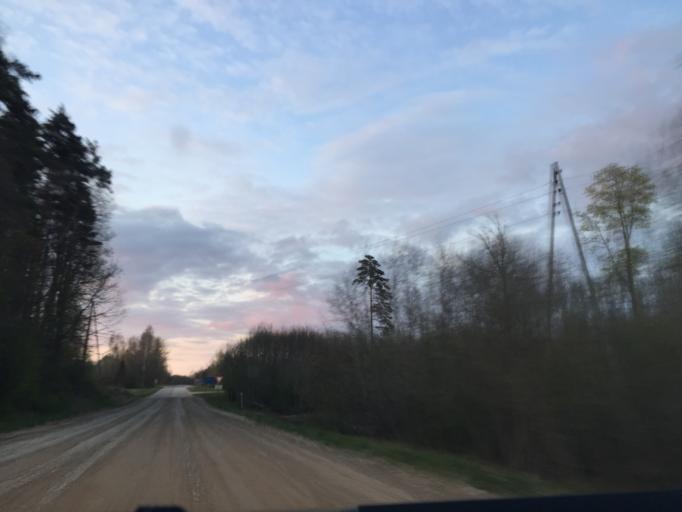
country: LV
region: Aluksnes Rajons
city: Aluksne
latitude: 57.3901
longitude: 27.0432
